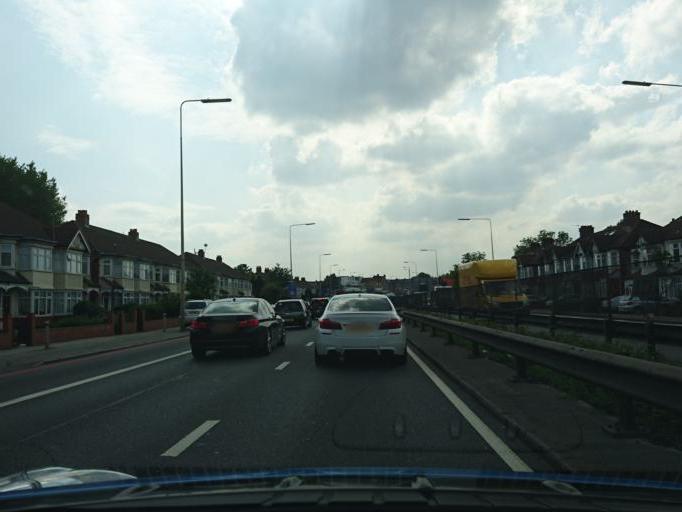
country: GB
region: England
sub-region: Greater London
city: Wood Green
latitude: 51.6134
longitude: -0.1046
